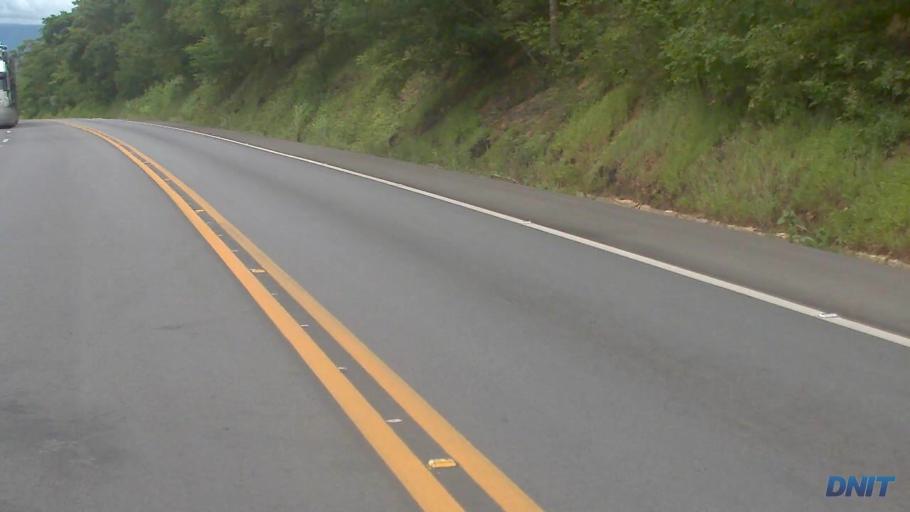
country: BR
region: Goias
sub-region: Posse
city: Posse
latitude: -14.3694
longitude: -46.4432
